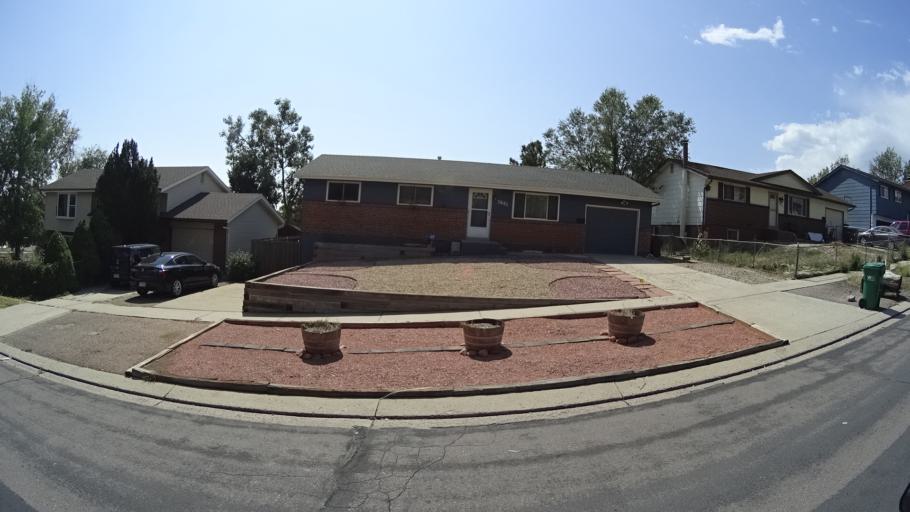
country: US
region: Colorado
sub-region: El Paso County
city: Stratmoor
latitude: 38.8283
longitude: -104.7631
